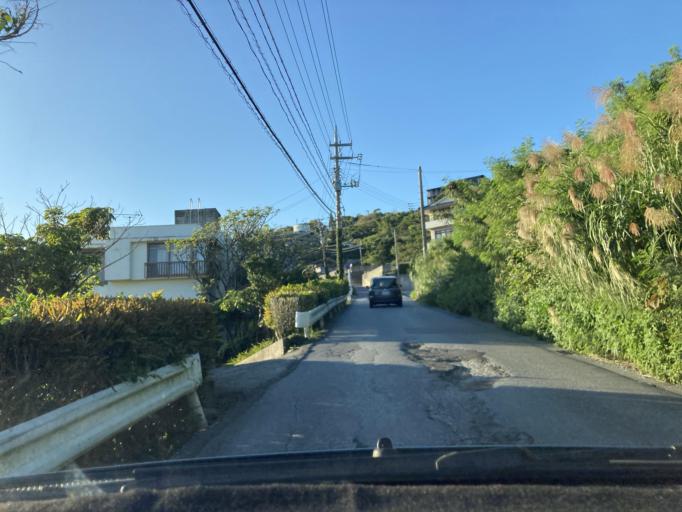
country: JP
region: Okinawa
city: Naha-shi
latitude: 26.2099
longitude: 127.7339
